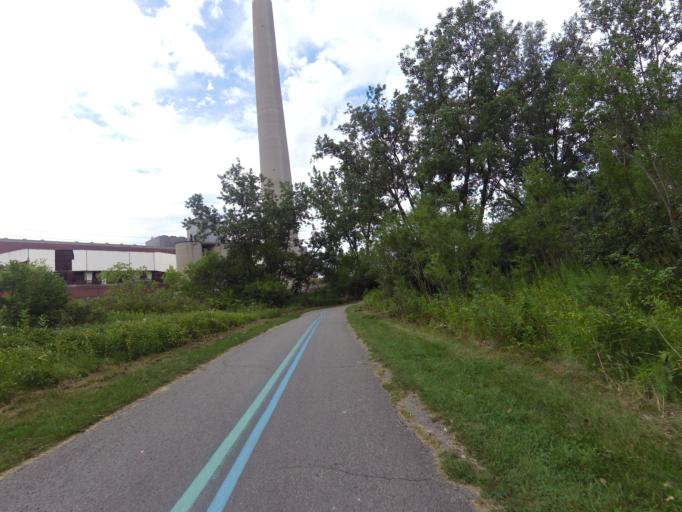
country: CA
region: Ontario
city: Toronto
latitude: 43.6448
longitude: -79.3338
